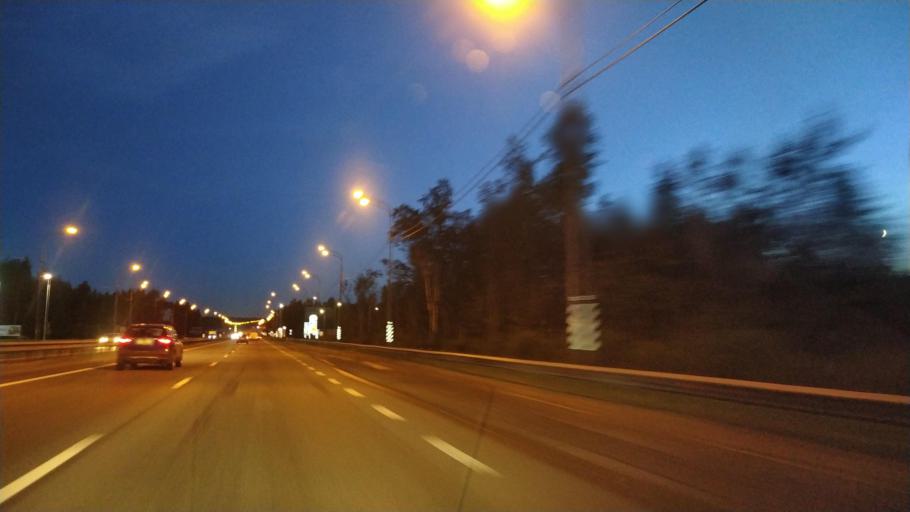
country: RU
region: Leningrad
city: Koltushi
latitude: 59.8939
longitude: 30.6572
